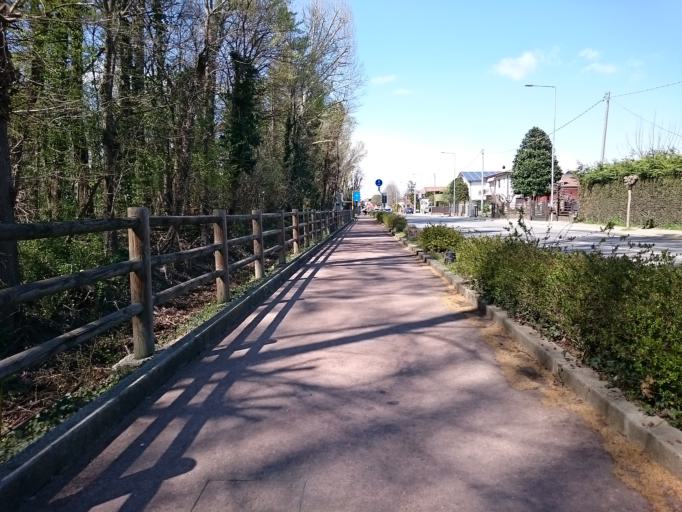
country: IT
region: Veneto
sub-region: Provincia di Padova
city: Brugine
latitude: 45.2924
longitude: 11.9974
